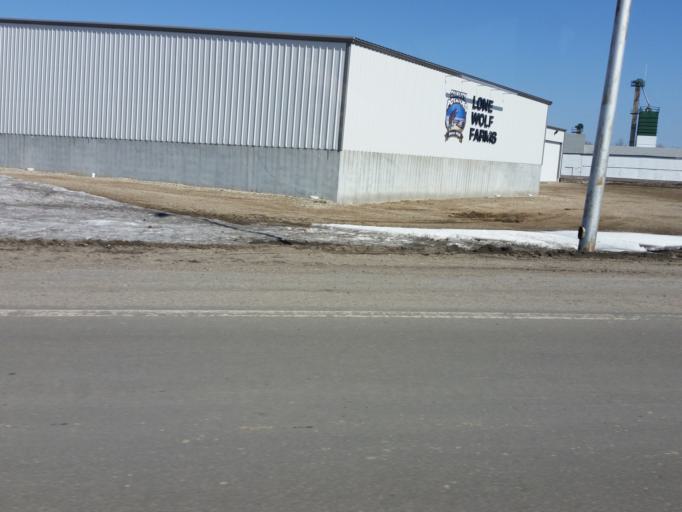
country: US
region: North Dakota
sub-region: Walsh County
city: Grafton
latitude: 48.2961
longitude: -97.3729
